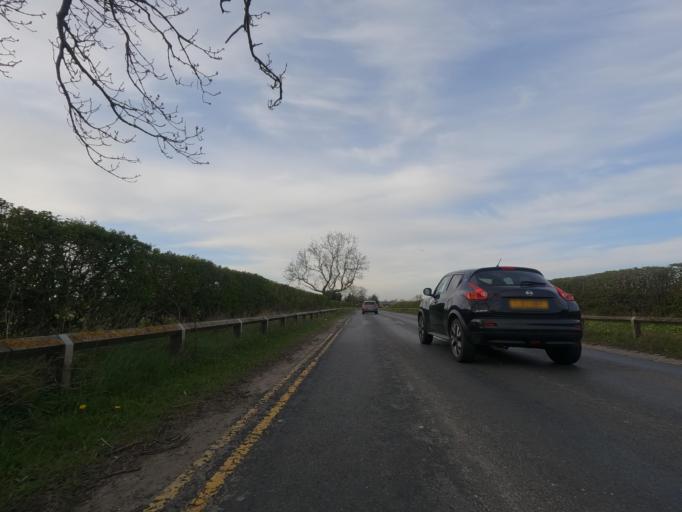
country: GB
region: England
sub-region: Newcastle upon Tyne
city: Dinnington
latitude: 55.0458
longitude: -1.6707
